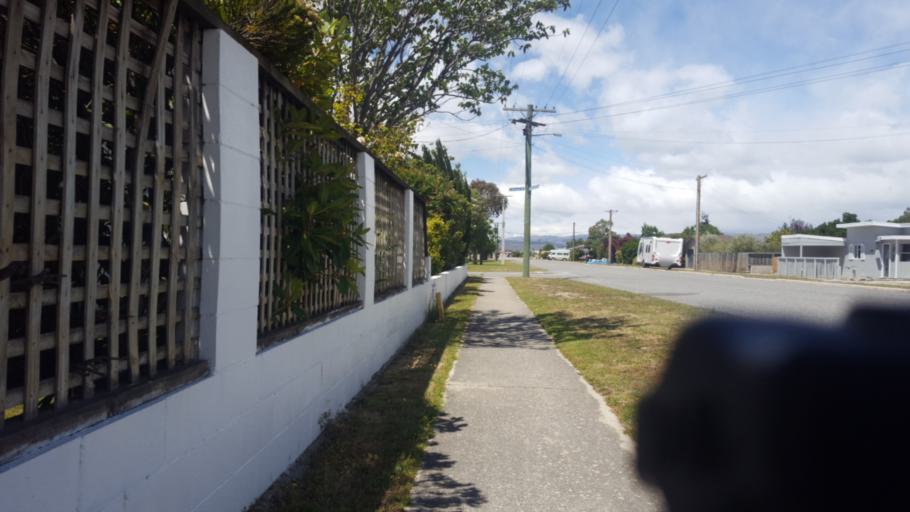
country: NZ
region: Otago
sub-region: Queenstown-Lakes District
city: Wanaka
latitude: -45.1909
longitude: 169.3241
